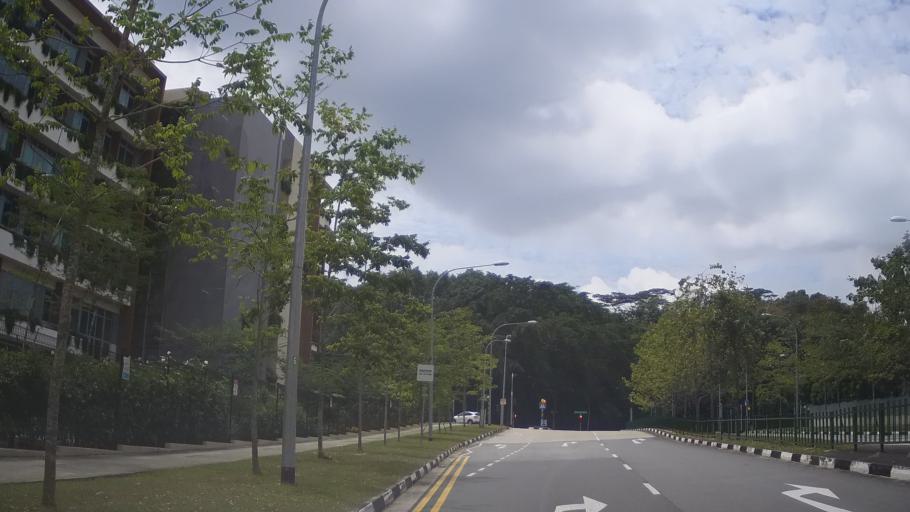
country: MY
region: Johor
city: Johor Bahru
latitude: 1.3655
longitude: 103.7722
